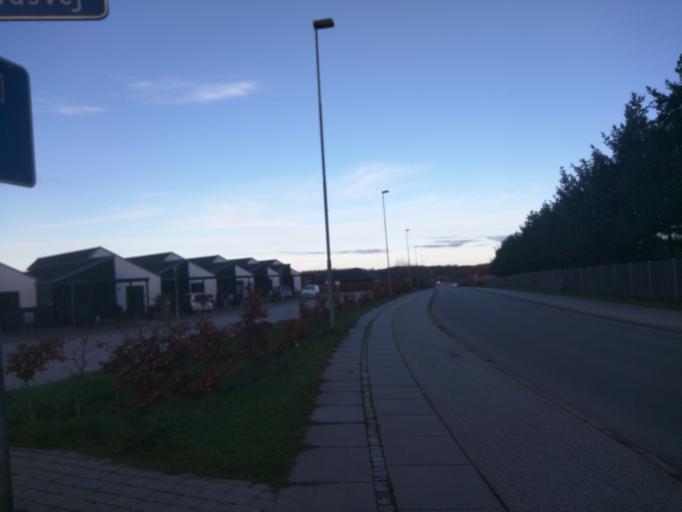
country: DK
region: Central Jutland
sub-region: Skanderborg Kommune
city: Horning
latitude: 56.0889
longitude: 10.0295
